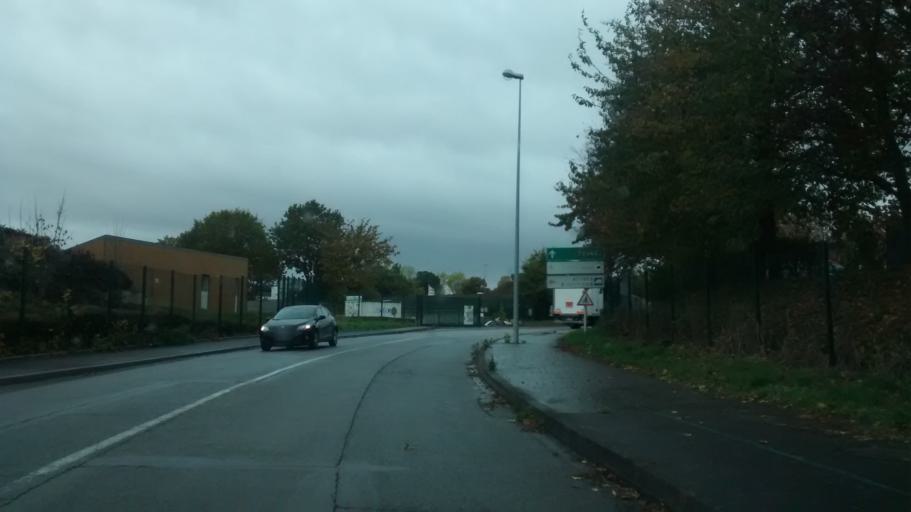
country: FR
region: Brittany
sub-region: Departement d'Ille-et-Vilaine
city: Noyal-sur-Vilaine
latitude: 48.1041
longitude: -1.5109
